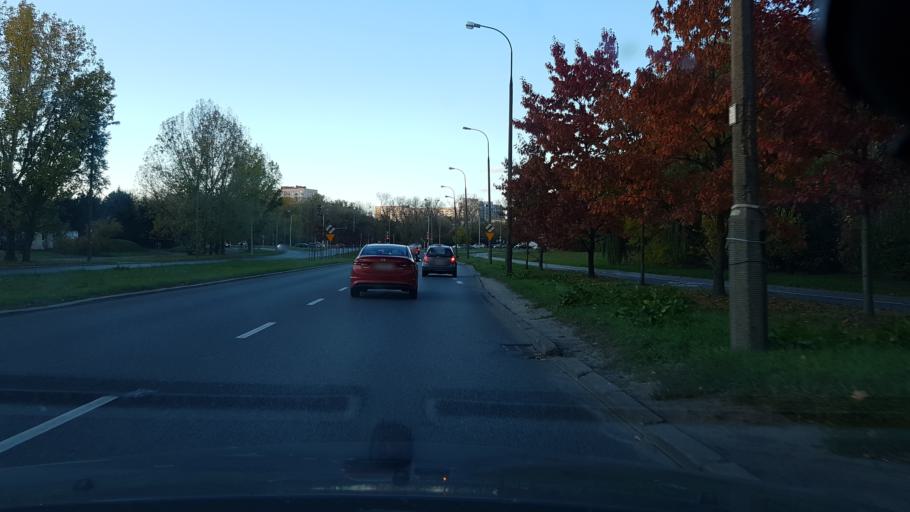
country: PL
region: Masovian Voivodeship
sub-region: Warszawa
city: Ursynow
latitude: 52.1655
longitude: 21.0353
